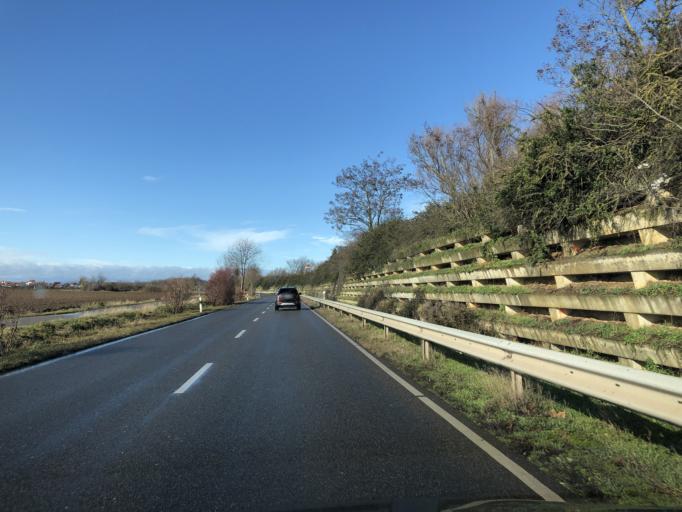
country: DE
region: Rheinland-Pfalz
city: Gartenstadt
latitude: 49.4503
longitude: 8.4012
